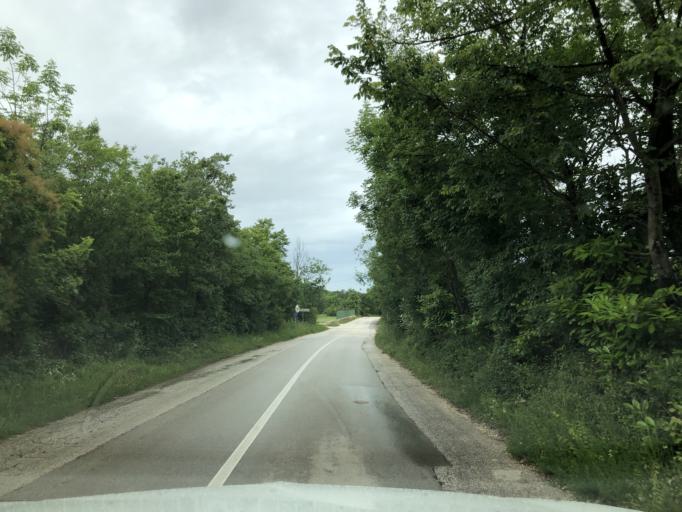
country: HR
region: Istarska
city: Buje
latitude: 45.4453
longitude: 13.6448
